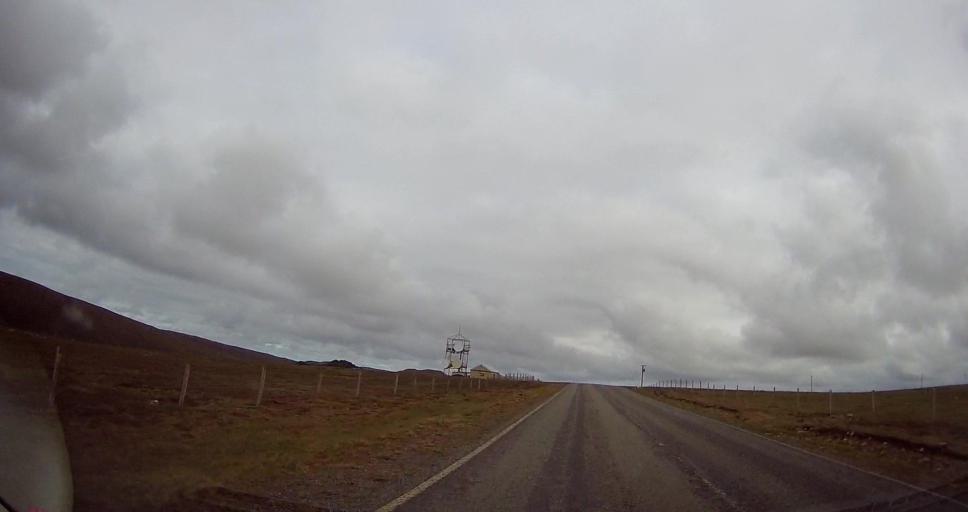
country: GB
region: Scotland
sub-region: Shetland Islands
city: Shetland
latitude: 60.7355
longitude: -0.8945
